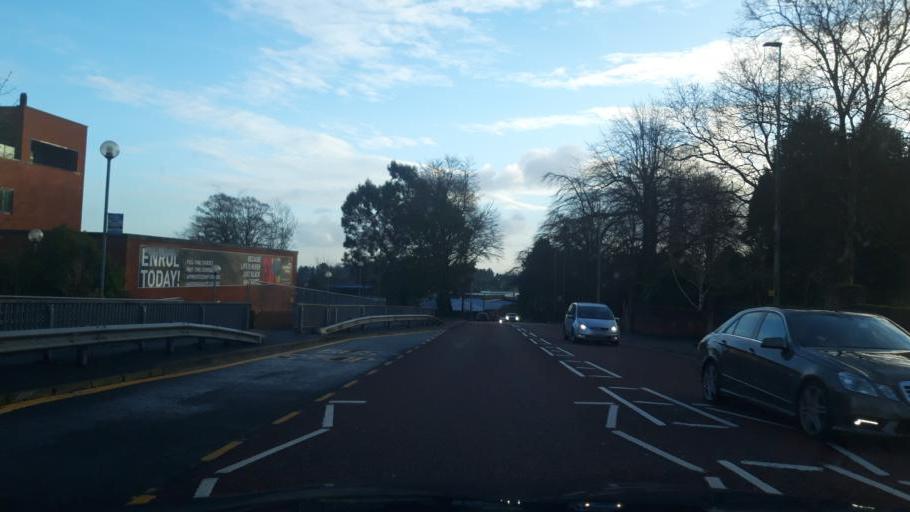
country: GB
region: Northern Ireland
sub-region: Dungannon District
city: Dungannon
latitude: 54.5087
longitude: -6.7644
